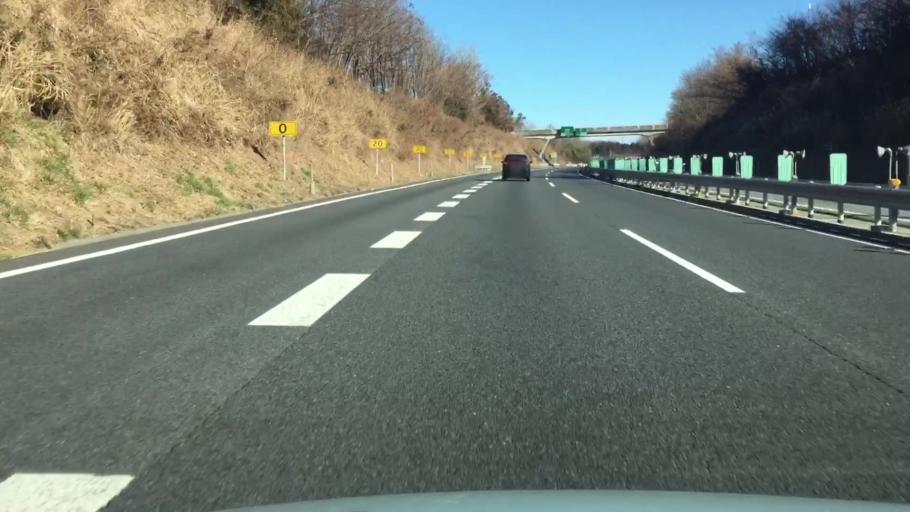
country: JP
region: Gunma
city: Shibukawa
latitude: 36.5265
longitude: 139.0411
